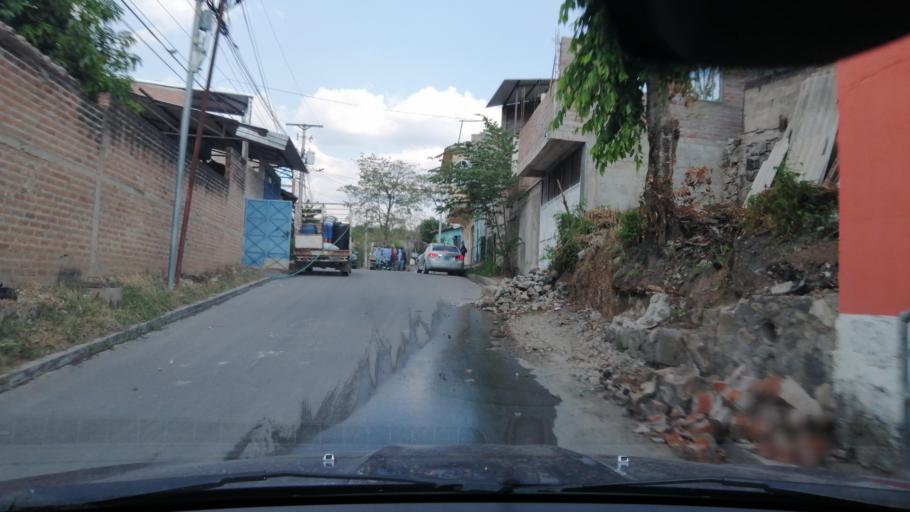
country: SV
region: Santa Ana
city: Metapan
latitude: 14.3298
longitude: -89.4359
